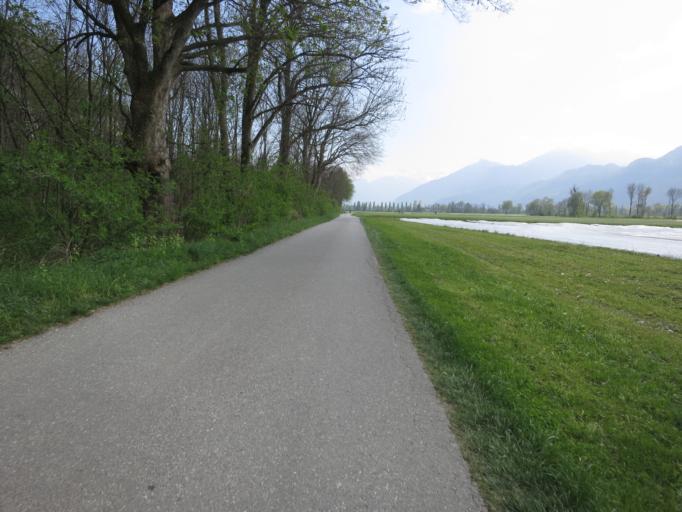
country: CH
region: Saint Gallen
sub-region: Wahlkreis Sarganserland
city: Sargans
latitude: 47.0477
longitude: 9.4723
